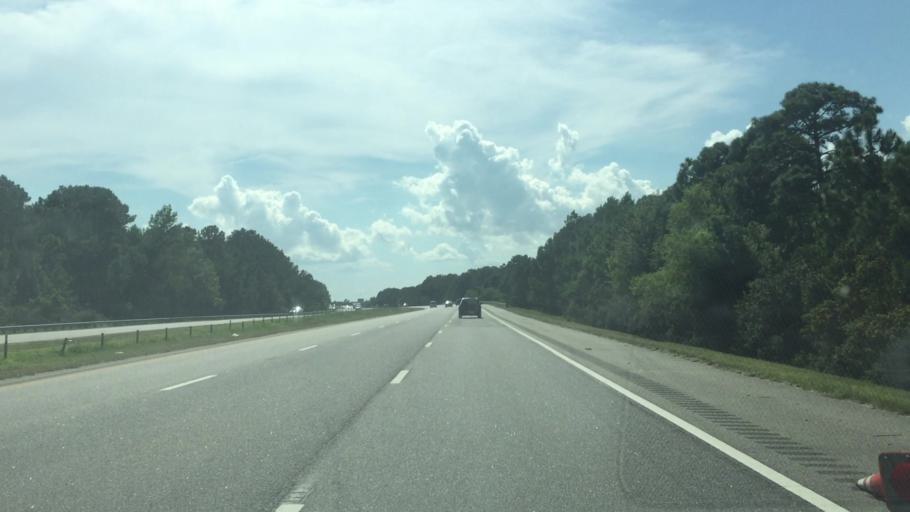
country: US
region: South Carolina
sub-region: Horry County
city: North Myrtle Beach
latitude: 33.8135
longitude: -78.7566
